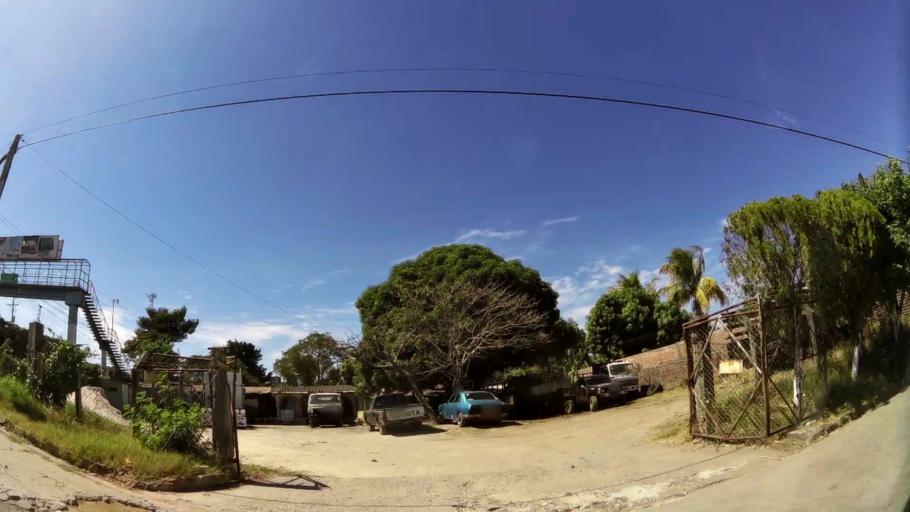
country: SV
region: Santa Ana
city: Chalchuapa
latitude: 13.9734
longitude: -89.7057
